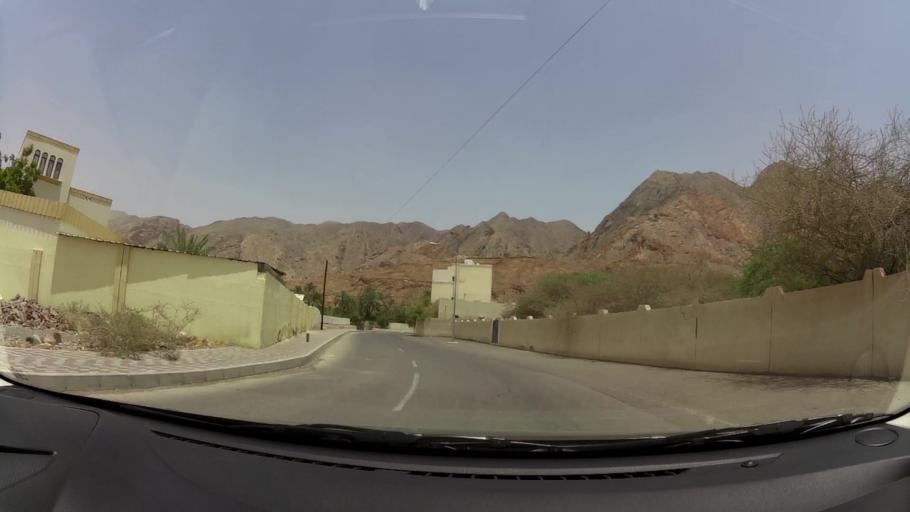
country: OM
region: Muhafazat Masqat
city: Bawshar
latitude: 23.5360
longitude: 58.3965
